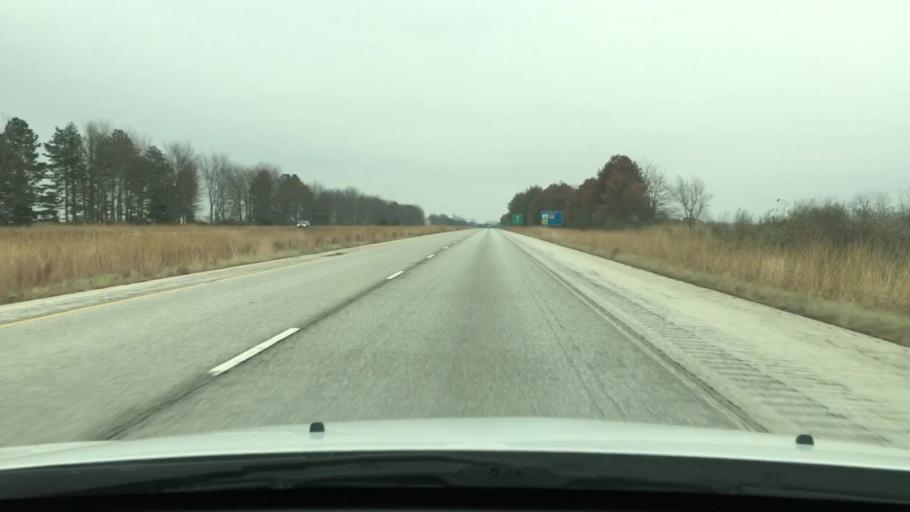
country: US
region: Illinois
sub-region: Morgan County
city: South Jacksonville
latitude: 39.6821
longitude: -90.2586
